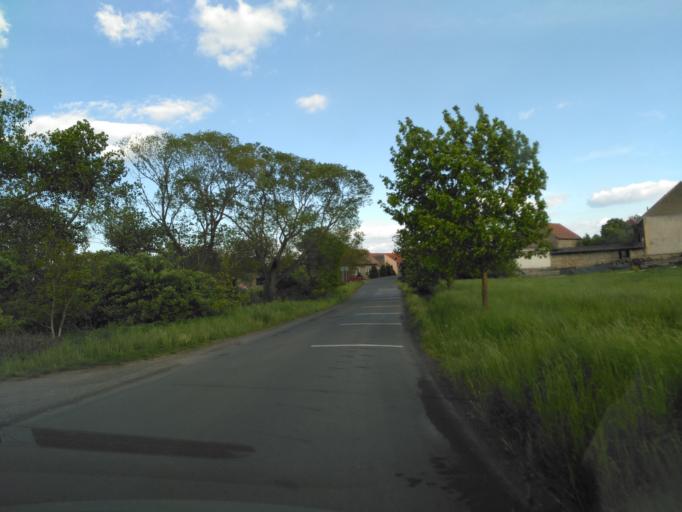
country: CZ
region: Central Bohemia
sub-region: Okres Beroun
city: Beroun
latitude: 49.9245
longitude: 14.0951
